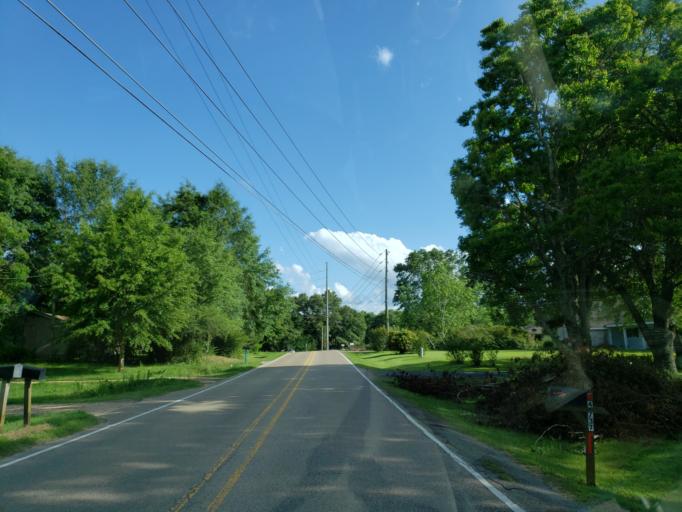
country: US
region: Mississippi
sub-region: Lamar County
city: West Hattiesburg
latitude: 31.2750
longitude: -89.4145
